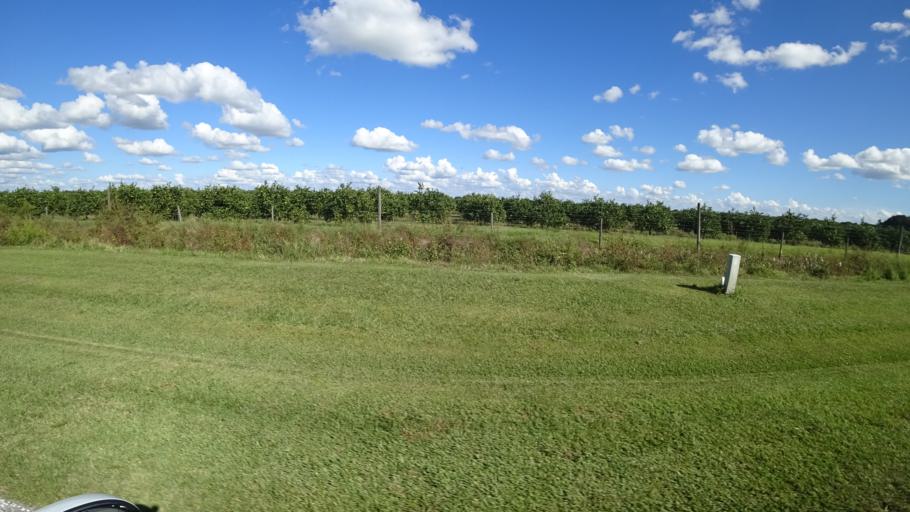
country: US
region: Florida
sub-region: Sarasota County
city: North Port
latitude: 27.2065
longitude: -82.1222
